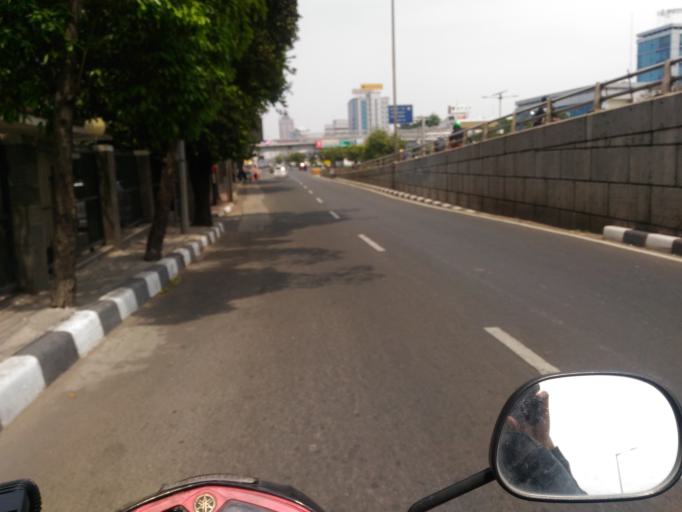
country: ID
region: Jakarta Raya
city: Jakarta
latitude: -6.2432
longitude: 106.8457
